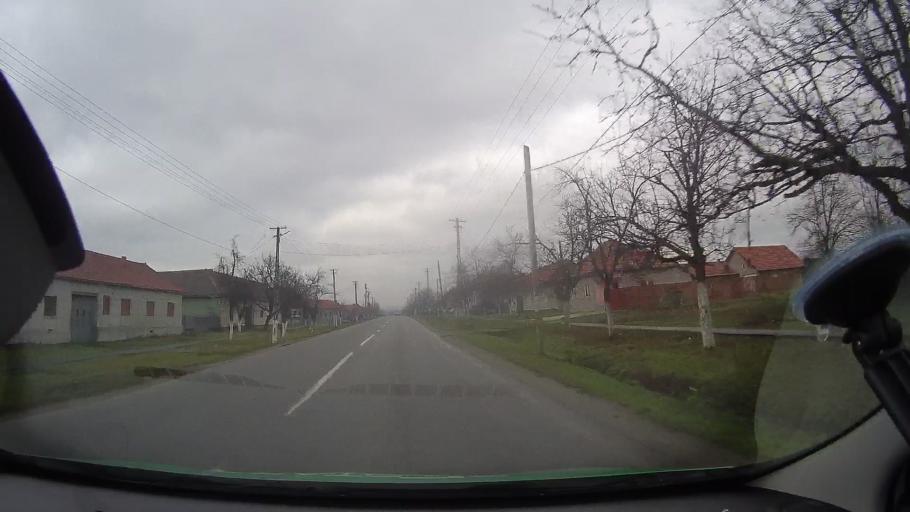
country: RO
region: Arad
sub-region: Comuna Almas
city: Almas
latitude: 46.2871
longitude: 22.2299
